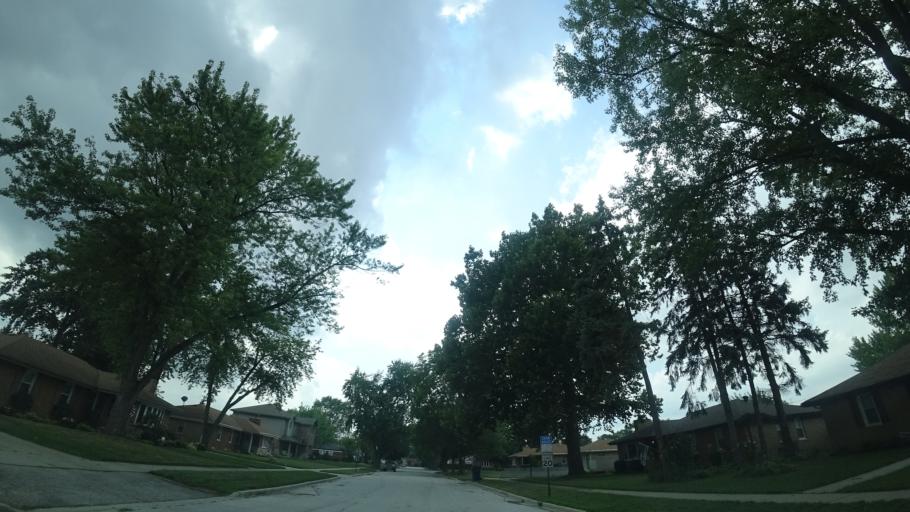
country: US
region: Illinois
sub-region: Cook County
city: Chicago Ridge
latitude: 41.6951
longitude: -87.7656
